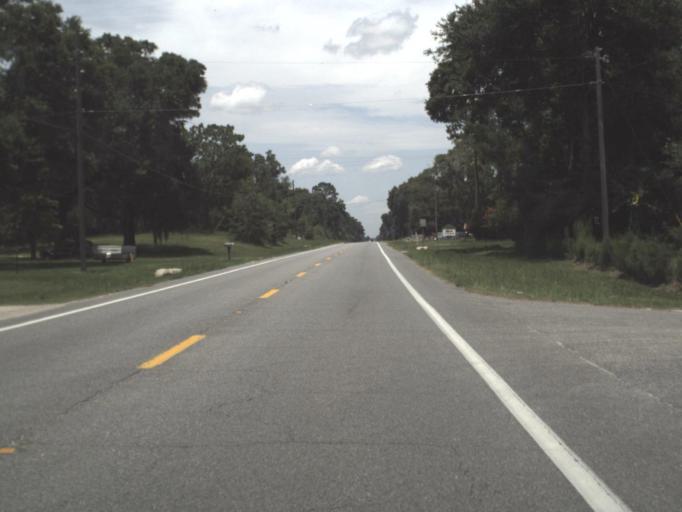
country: US
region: Florida
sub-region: Lafayette County
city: Mayo
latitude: 30.0597
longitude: -83.1752
